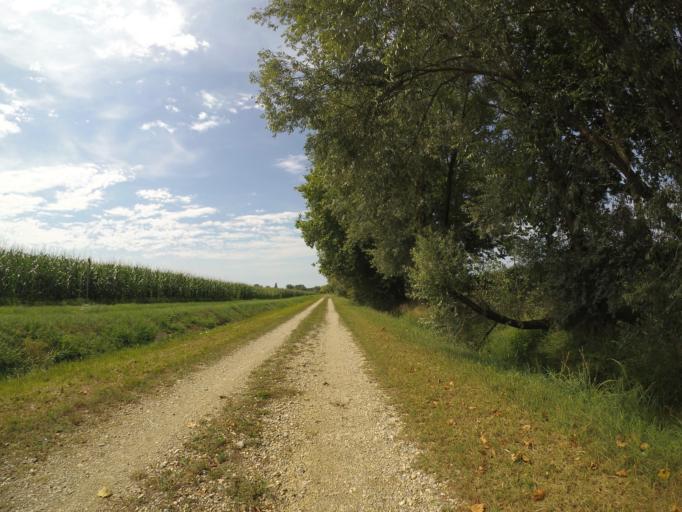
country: IT
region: Friuli Venezia Giulia
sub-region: Provincia di Udine
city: Codroipo
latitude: 45.9424
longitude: 13.0044
